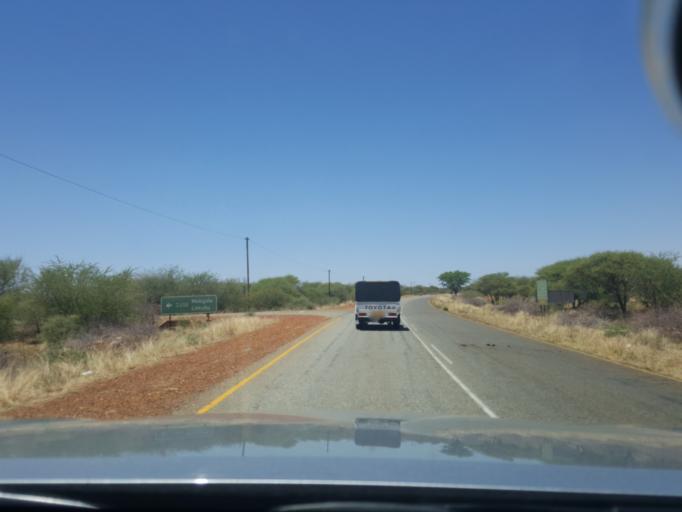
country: BW
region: South East
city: Otse
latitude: -25.1007
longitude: 25.9619
